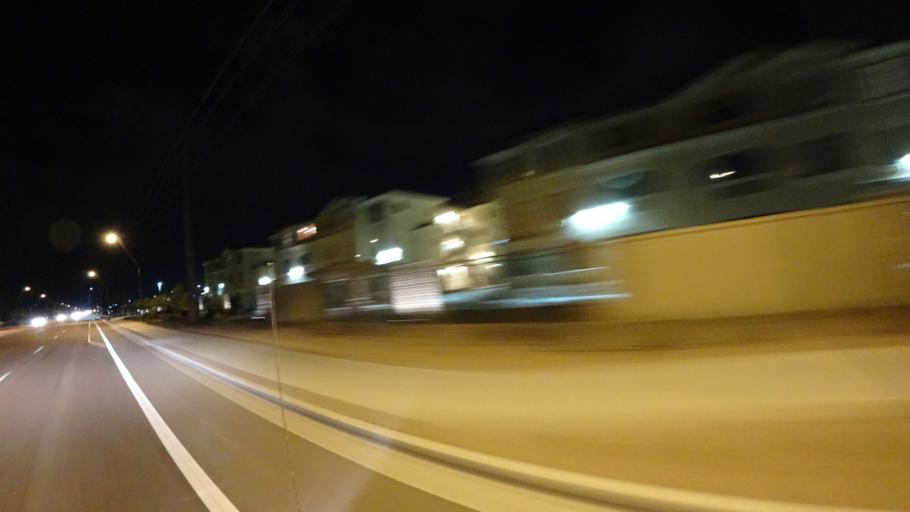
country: US
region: Arizona
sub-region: Maricopa County
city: Guadalupe
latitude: 33.3302
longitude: -111.9633
